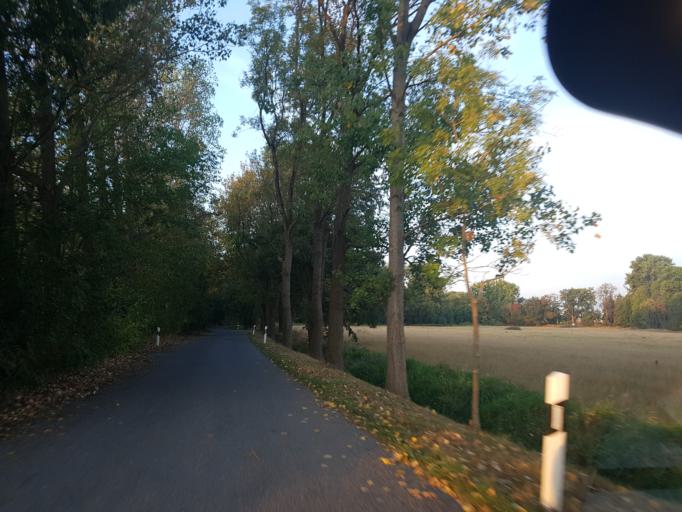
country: DE
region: Saxony
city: Strehla
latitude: 51.3080
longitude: 13.1858
